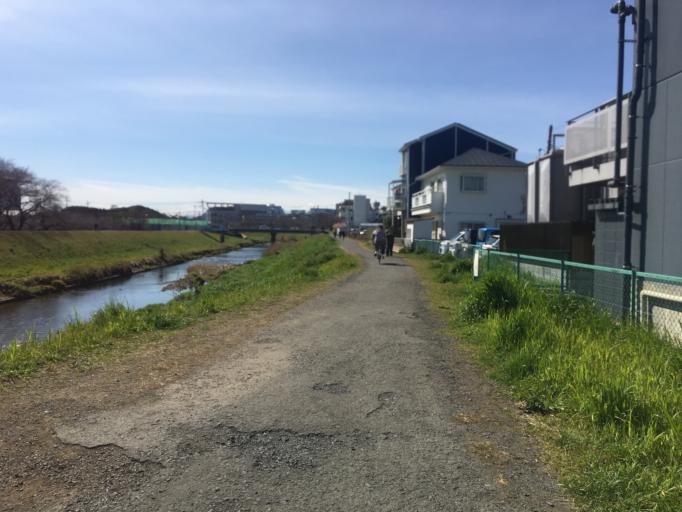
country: JP
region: Saitama
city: Asaka
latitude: 35.8163
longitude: 139.5938
